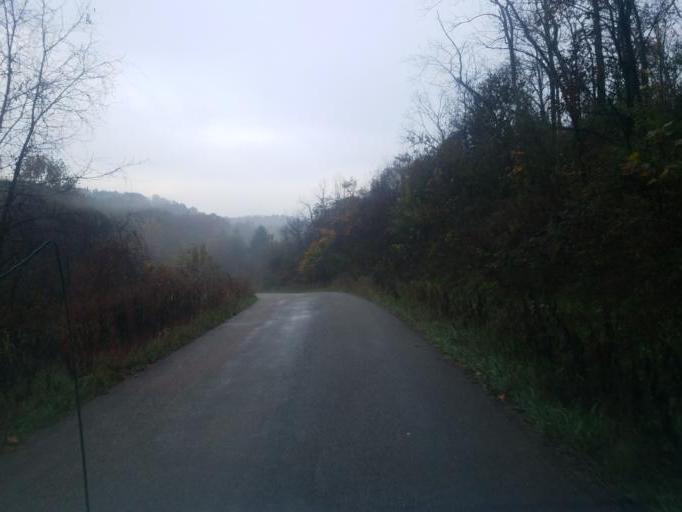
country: US
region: Ohio
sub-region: Athens County
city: Glouster
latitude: 39.5028
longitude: -81.9519
